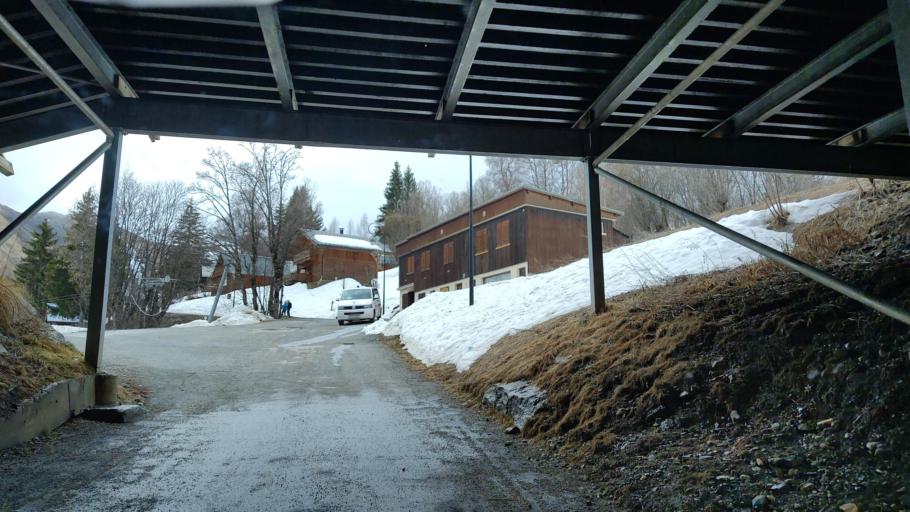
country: FR
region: Rhone-Alpes
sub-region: Departement de la Savoie
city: Saint-Jean-de-Maurienne
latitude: 45.2196
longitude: 6.2233
